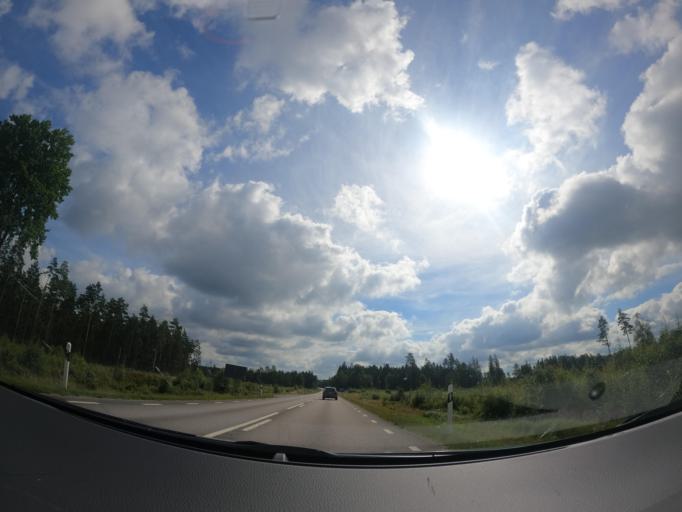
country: SE
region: Halland
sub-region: Hylte Kommun
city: Hyltebruk
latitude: 57.1290
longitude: 13.2319
